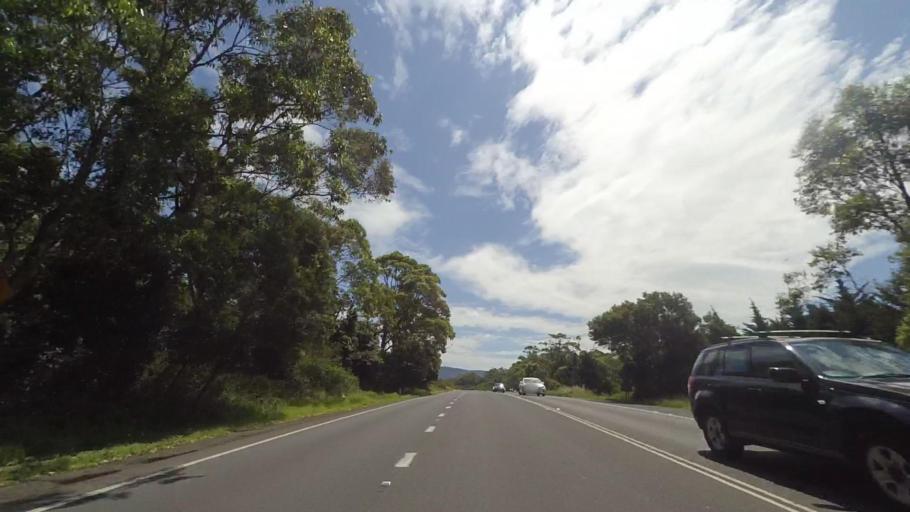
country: AU
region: New South Wales
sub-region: Kiama
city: Gerringong
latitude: -34.7439
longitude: 150.7731
